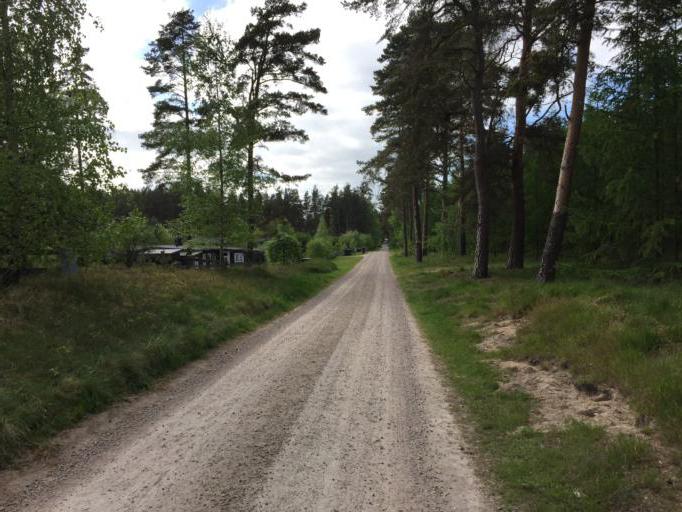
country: SE
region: Skane
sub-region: Sjobo Kommun
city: Sjoebo
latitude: 55.6657
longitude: 13.6356
